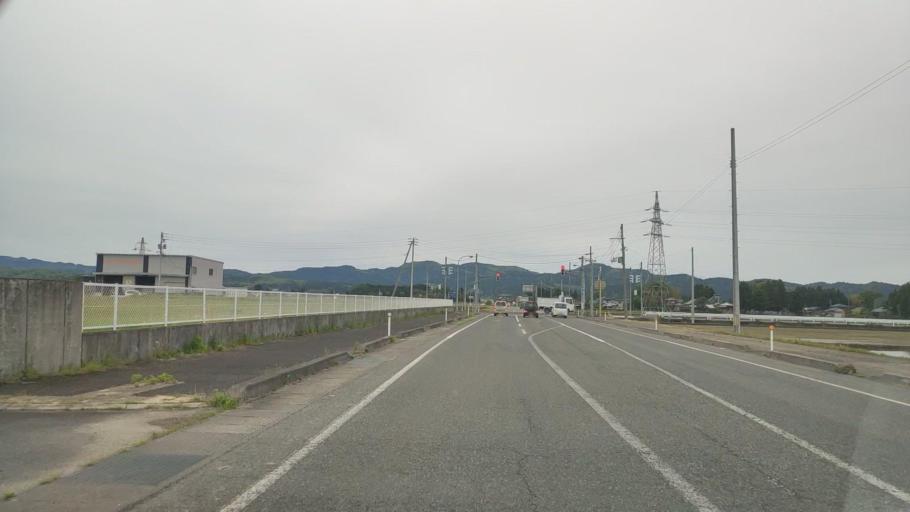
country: JP
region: Niigata
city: Gosen
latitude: 37.7293
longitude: 139.1673
